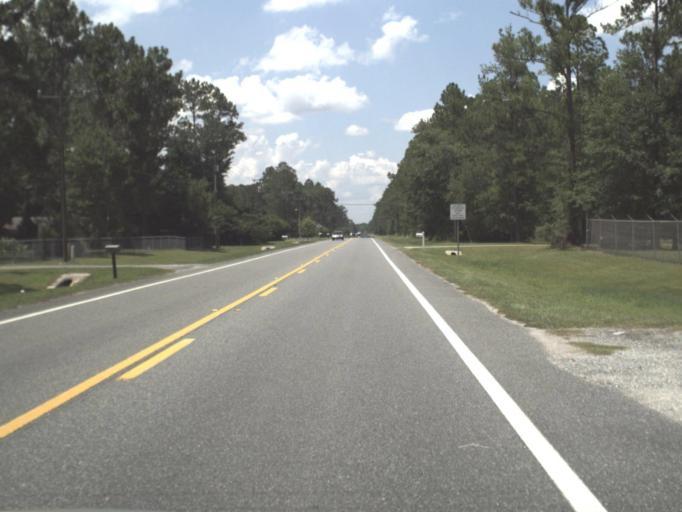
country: US
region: Florida
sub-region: Baker County
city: Macclenny
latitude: 30.3027
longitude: -82.1257
